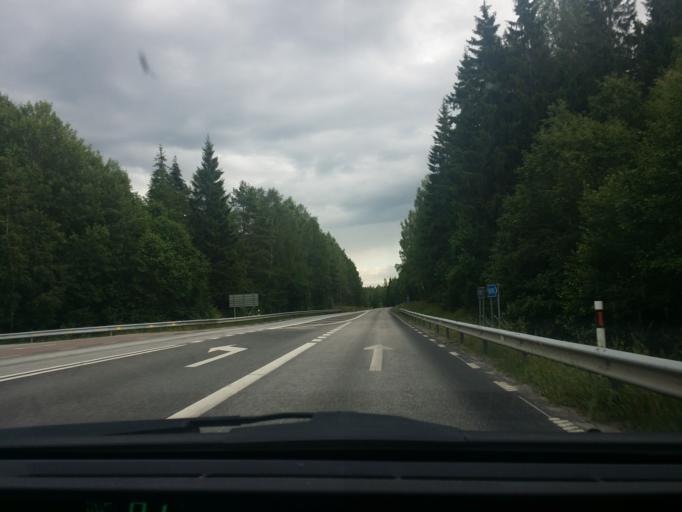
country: SE
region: OErebro
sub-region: Nora Kommun
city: Nora
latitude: 59.4903
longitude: 15.0596
